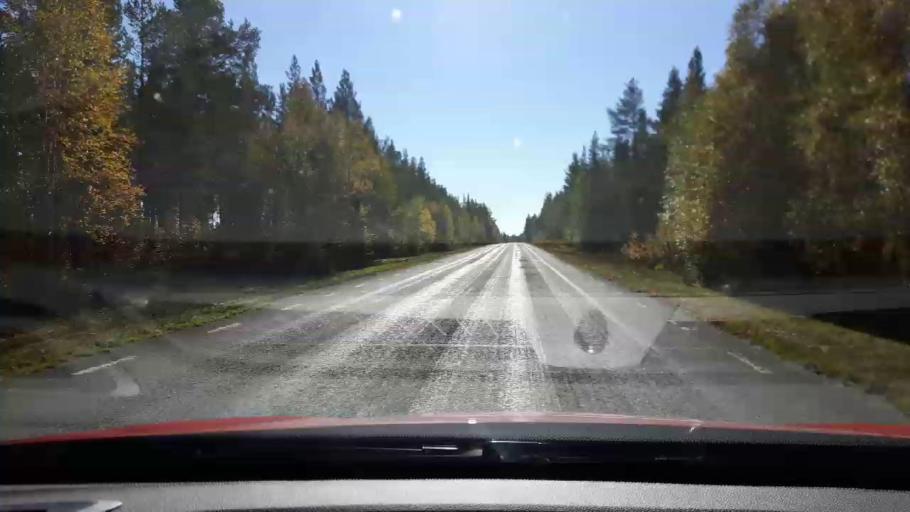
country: SE
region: Jaemtland
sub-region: Harjedalens Kommun
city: Sveg
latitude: 62.3459
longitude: 14.0345
